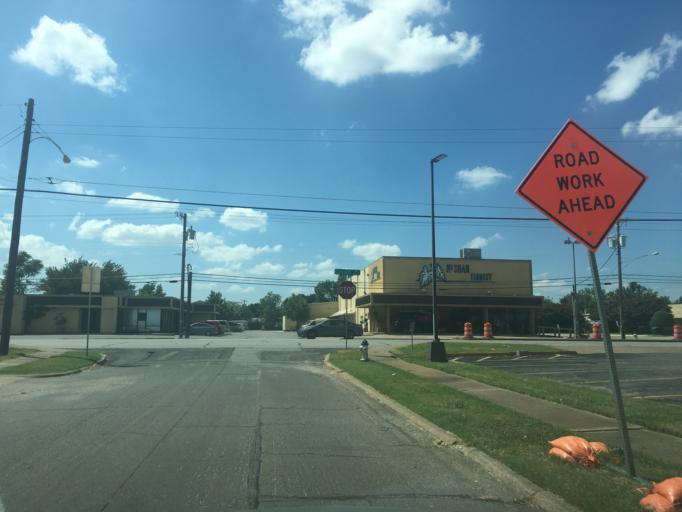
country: US
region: Texas
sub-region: Dallas County
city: Garland
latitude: 32.8409
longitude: -96.6924
